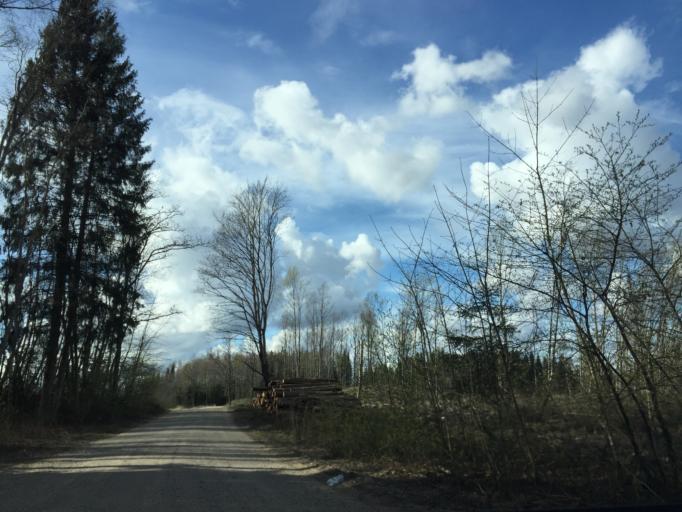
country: LV
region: Burtnieki
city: Matisi
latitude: 57.6065
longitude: 25.0443
